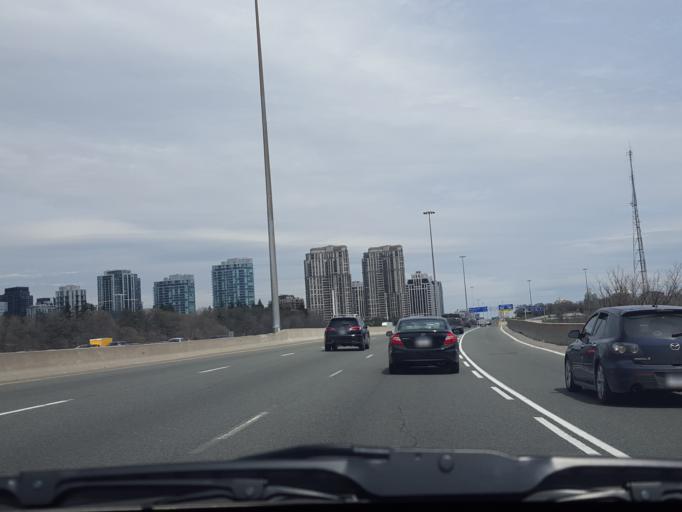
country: CA
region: Ontario
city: North York
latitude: 43.7490
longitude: -79.4145
